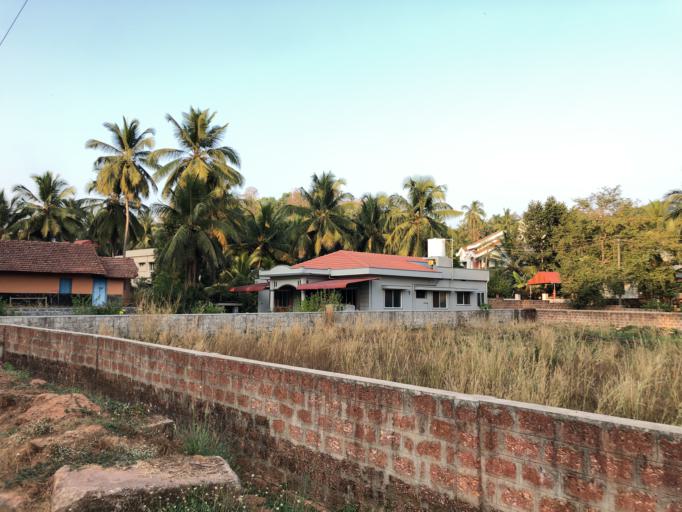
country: IN
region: Karnataka
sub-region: Dakshina Kannada
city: Mangalore
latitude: 12.8719
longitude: 74.8743
